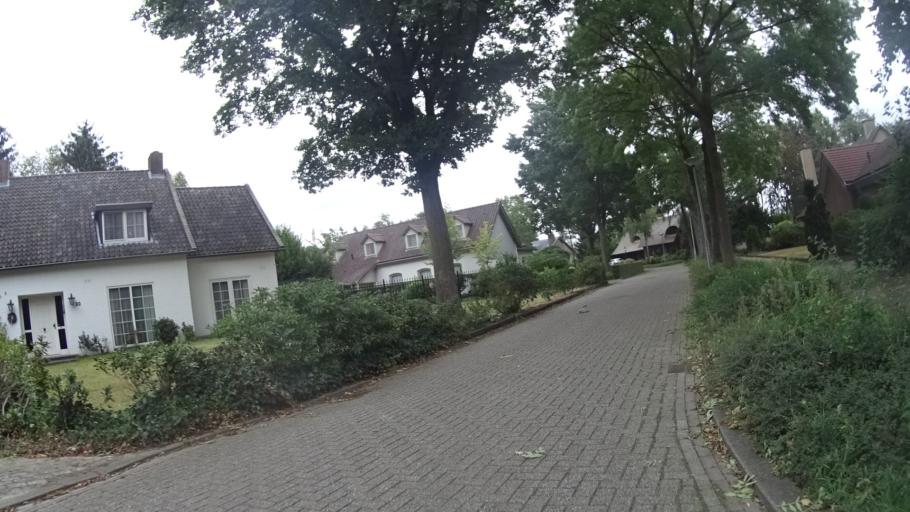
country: NL
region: Limburg
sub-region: Gemeente Venlo
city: Tegelen
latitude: 51.3549
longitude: 6.1379
